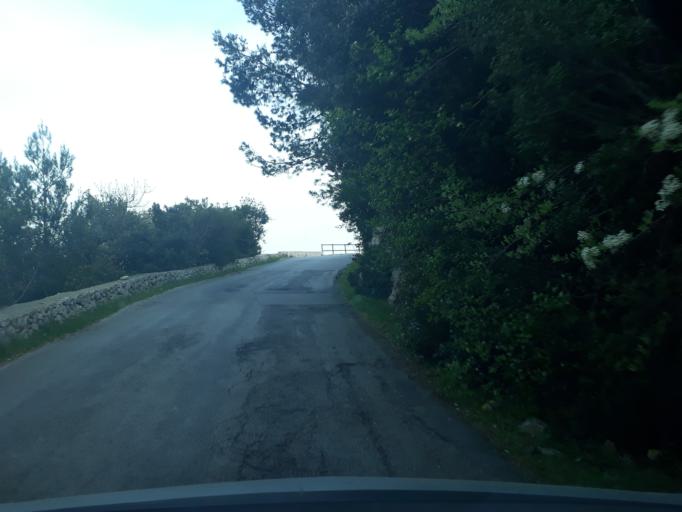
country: IT
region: Apulia
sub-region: Provincia di Brindisi
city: Lamie di Olimpie-Selva
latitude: 40.8298
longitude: 17.3360
